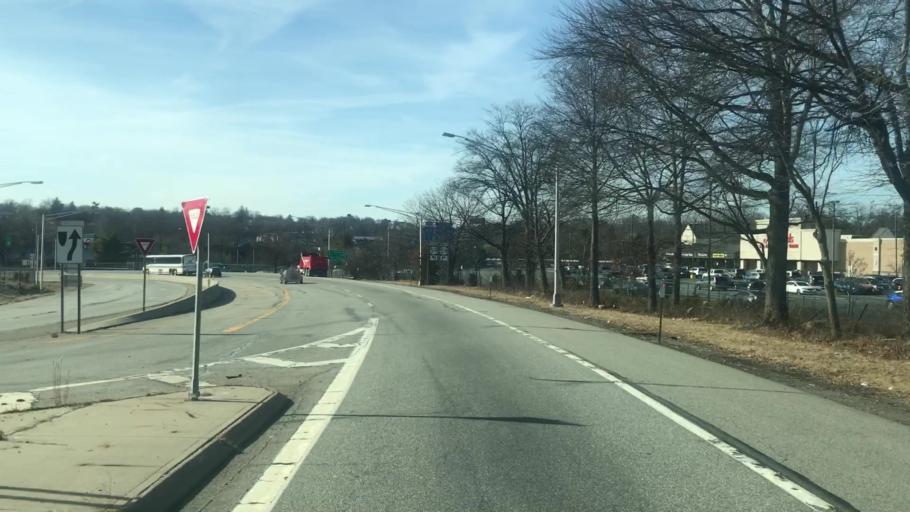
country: US
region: New York
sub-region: Rockland County
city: Spring Valley
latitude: 41.1047
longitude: -74.0270
